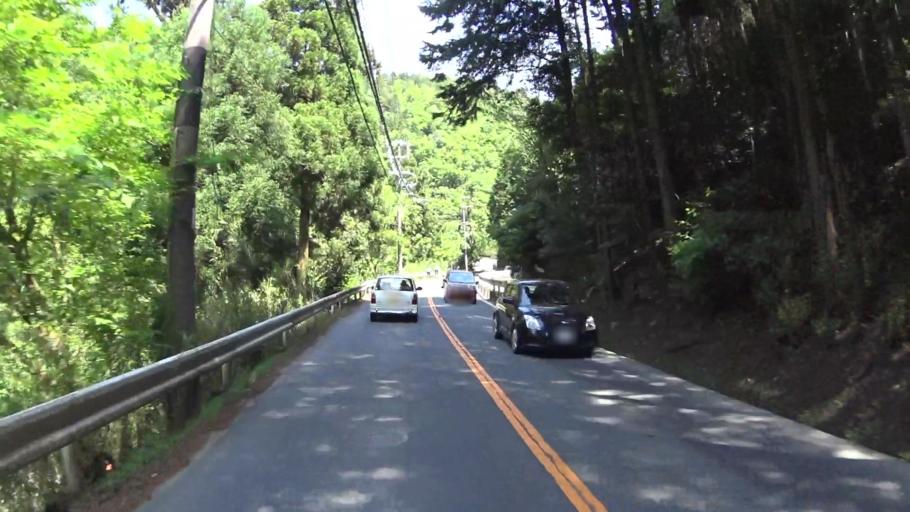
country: JP
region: Kyoto
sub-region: Kyoto-shi
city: Kamigyo-ku
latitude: 35.0949
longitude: 135.8203
